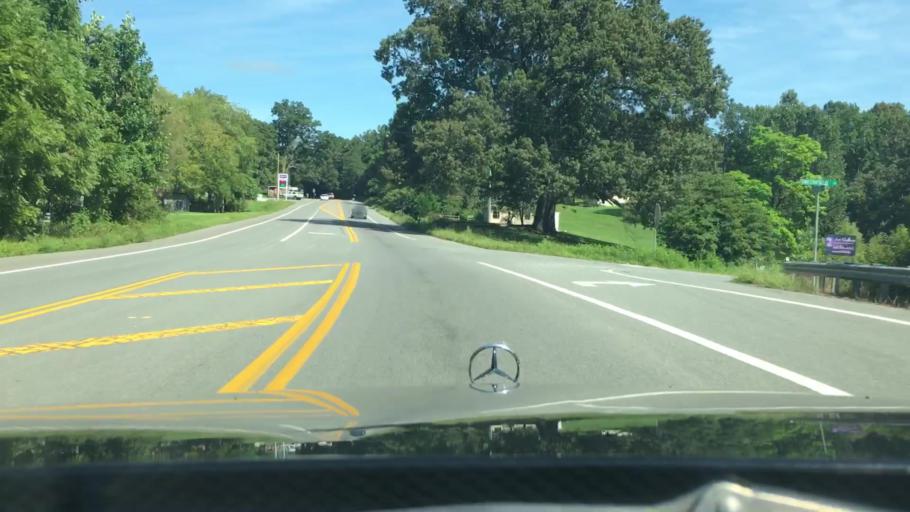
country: US
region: Virginia
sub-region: Nelson County
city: Nellysford
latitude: 37.9288
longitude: -78.8380
